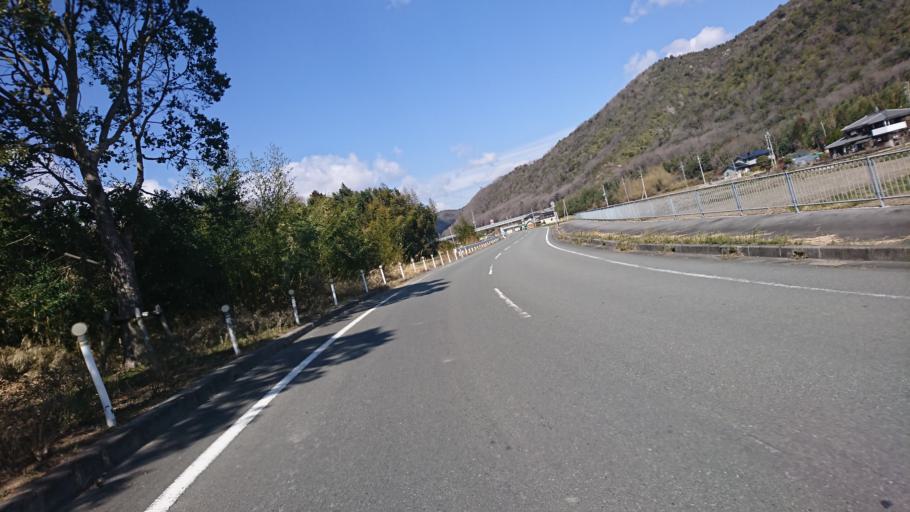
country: JP
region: Hyogo
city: Kakogawacho-honmachi
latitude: 34.8429
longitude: 134.8160
